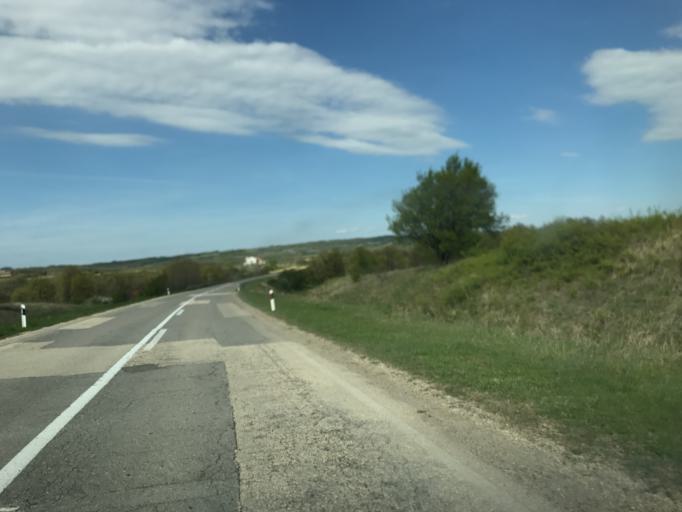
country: RS
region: Central Serbia
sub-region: Zajecarski Okrug
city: Zajecar
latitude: 44.0838
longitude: 22.3382
